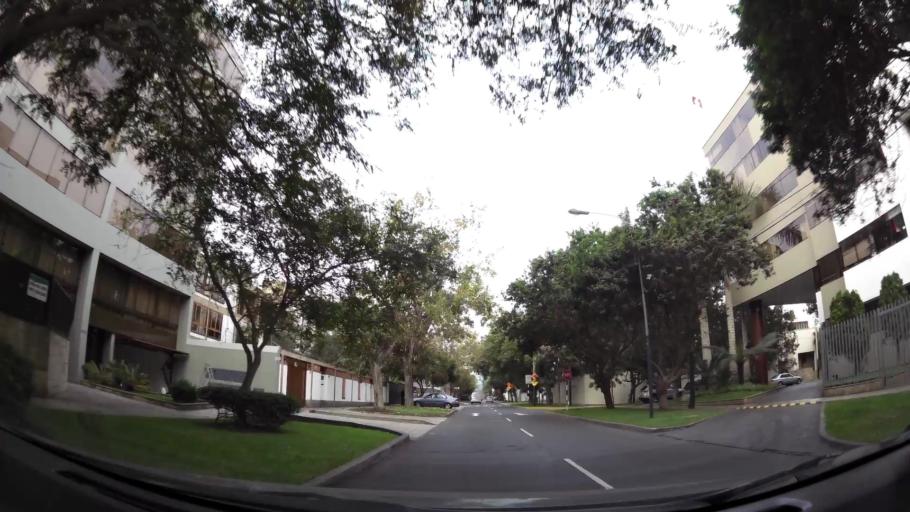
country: PE
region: Lima
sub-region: Lima
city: San Isidro
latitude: -12.1046
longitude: -77.0442
